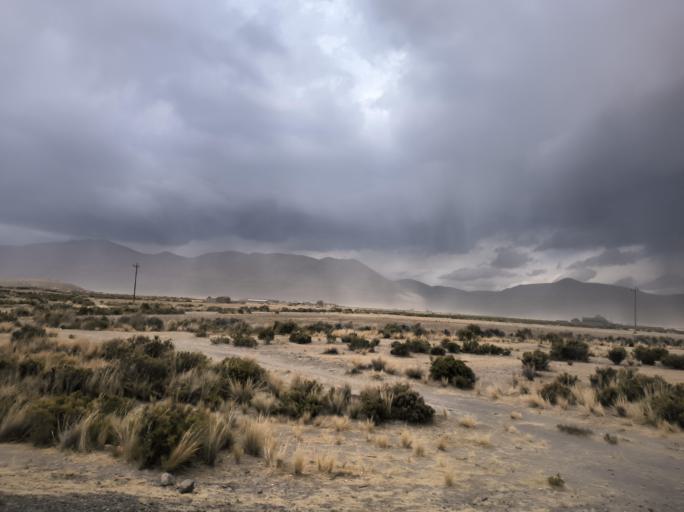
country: BO
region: Oruro
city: Challapata
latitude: -18.7729
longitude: -66.8550
